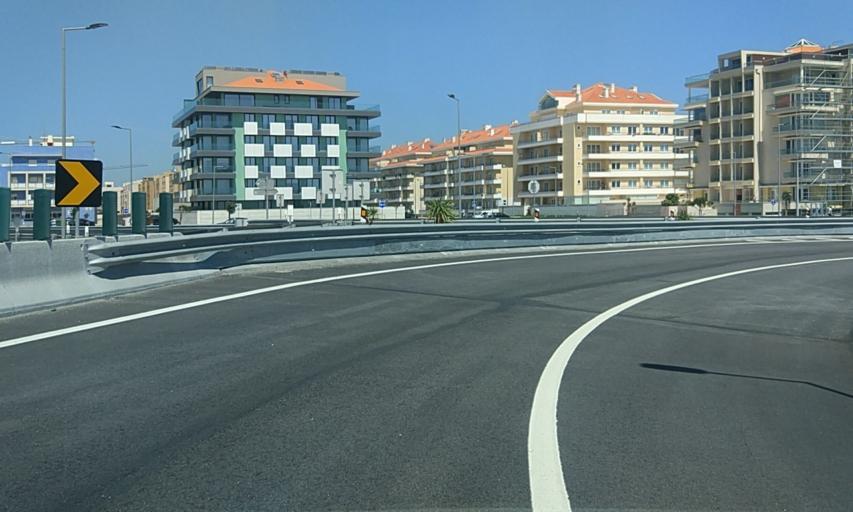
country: PT
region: Aveiro
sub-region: Ilhavo
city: Gafanha da Encarnacao
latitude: 40.6321
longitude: -8.7465
